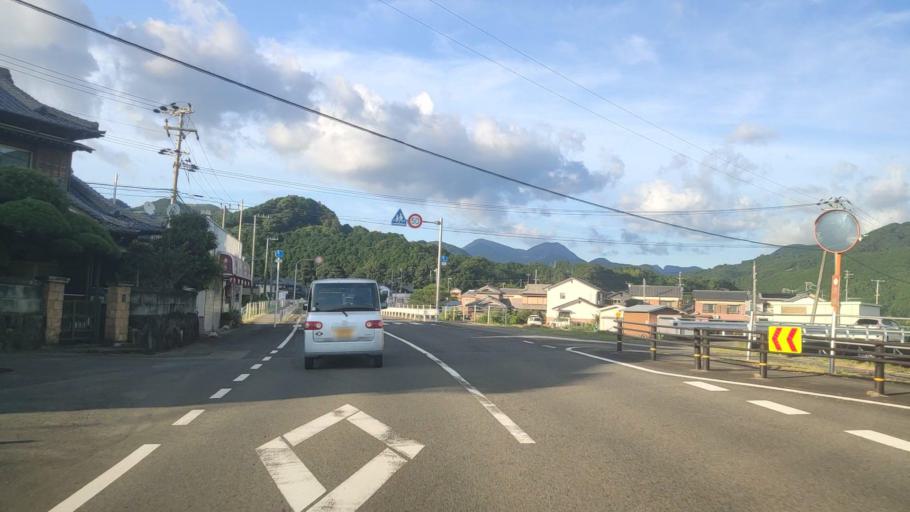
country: JP
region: Wakayama
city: Tanabe
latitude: 33.7169
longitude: 135.4707
